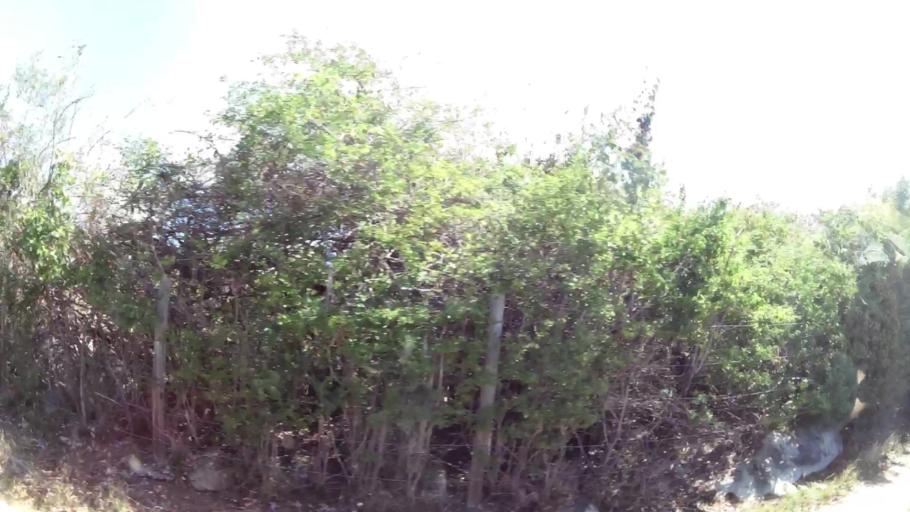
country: VG
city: Tortola
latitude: 18.4318
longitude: -64.4406
